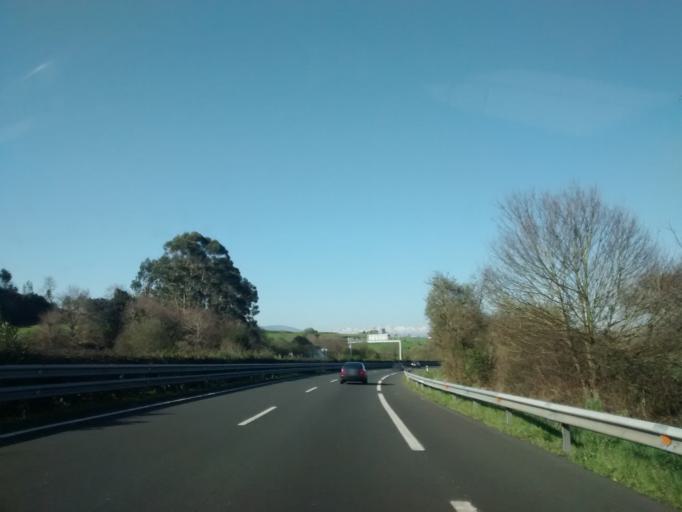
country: ES
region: Cantabria
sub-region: Provincia de Cantabria
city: Miengo
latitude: 43.4012
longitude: -3.9930
